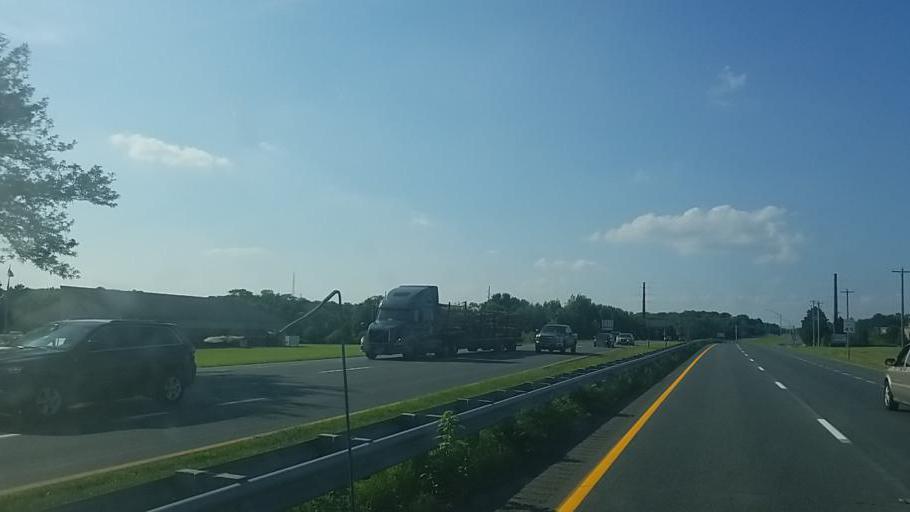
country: US
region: Maryland
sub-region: Worcester County
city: Berlin
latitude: 38.3357
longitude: -75.2112
